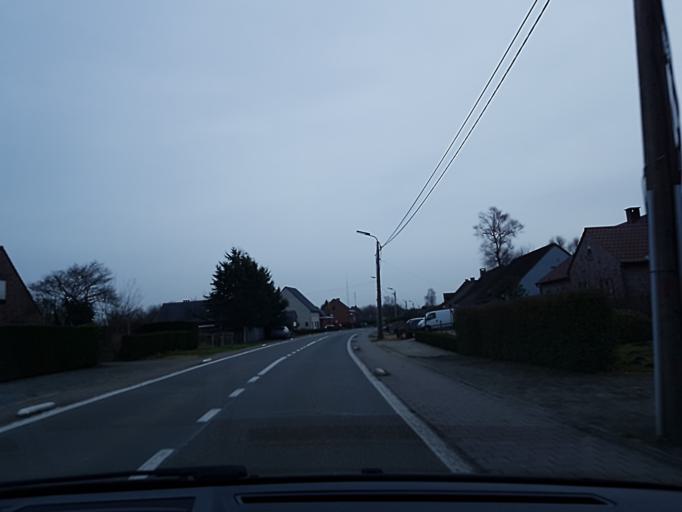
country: BE
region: Flanders
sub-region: Provincie Vlaams-Brabant
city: Keerbergen
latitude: 51.0179
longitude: 4.6487
